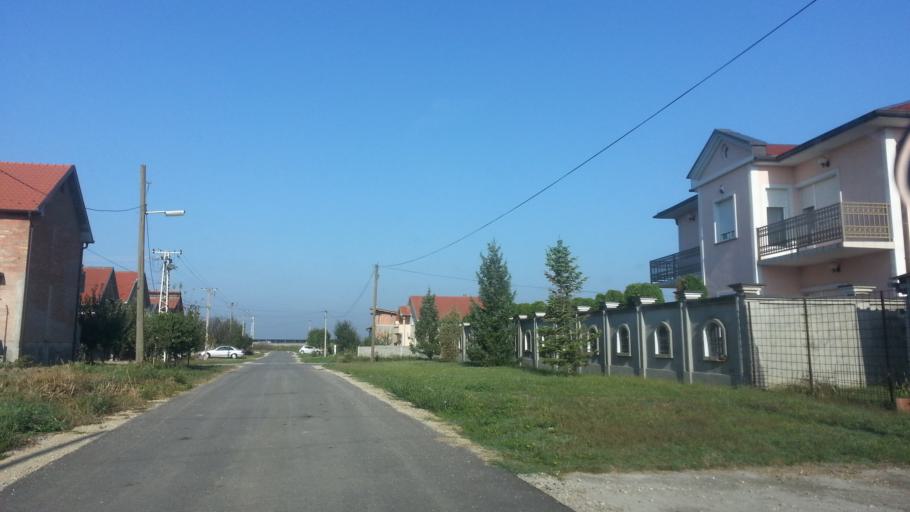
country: RS
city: Stari Banovci
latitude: 44.9868
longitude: 20.2701
